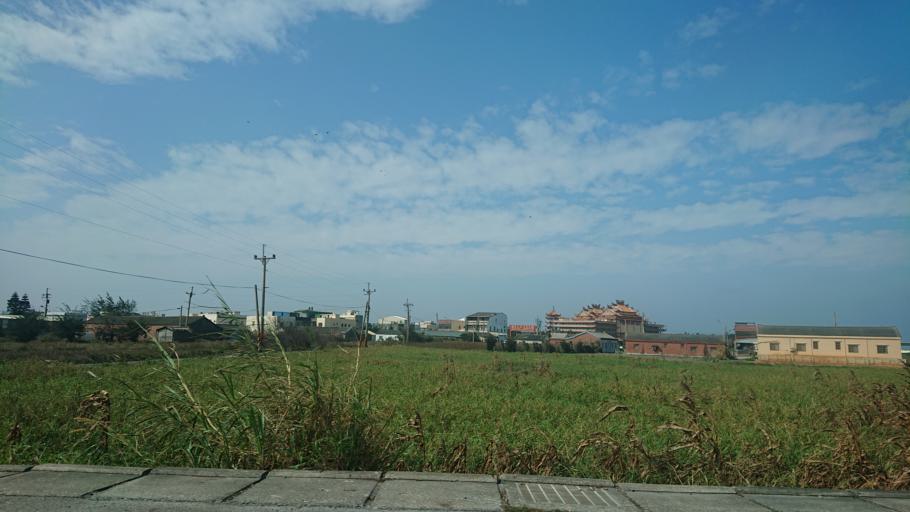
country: TW
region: Taiwan
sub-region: Changhua
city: Chang-hua
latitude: 23.9290
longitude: 120.3220
